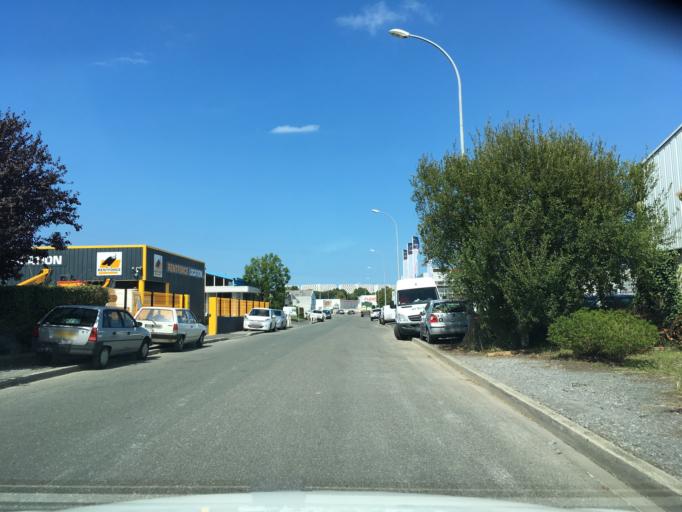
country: FR
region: Aquitaine
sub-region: Departement des Pyrenees-Atlantiques
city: Bayonne
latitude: 43.4880
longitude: -1.4508
